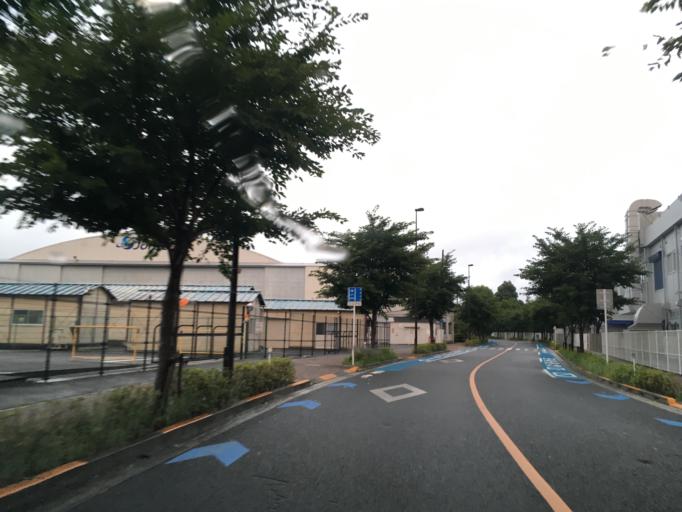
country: JP
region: Tokyo
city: Chofugaoka
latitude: 35.6741
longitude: 139.5290
